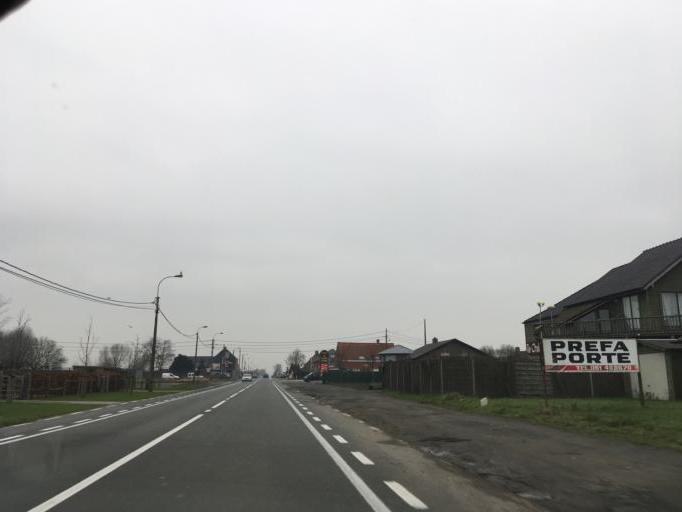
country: BE
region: Flanders
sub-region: Provincie West-Vlaanderen
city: Ingelmunster
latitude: 50.9505
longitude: 3.2468
